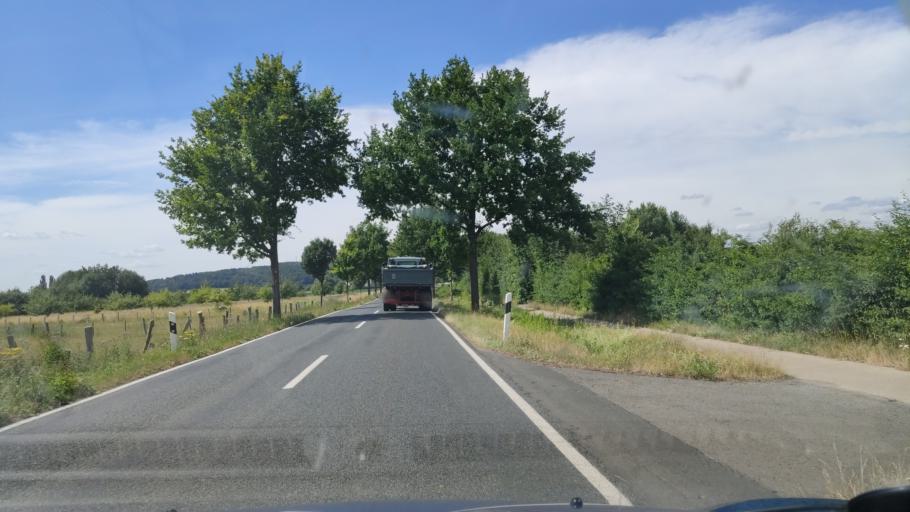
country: DE
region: Lower Saxony
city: Ronnenberg
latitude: 52.3234
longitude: 9.6454
